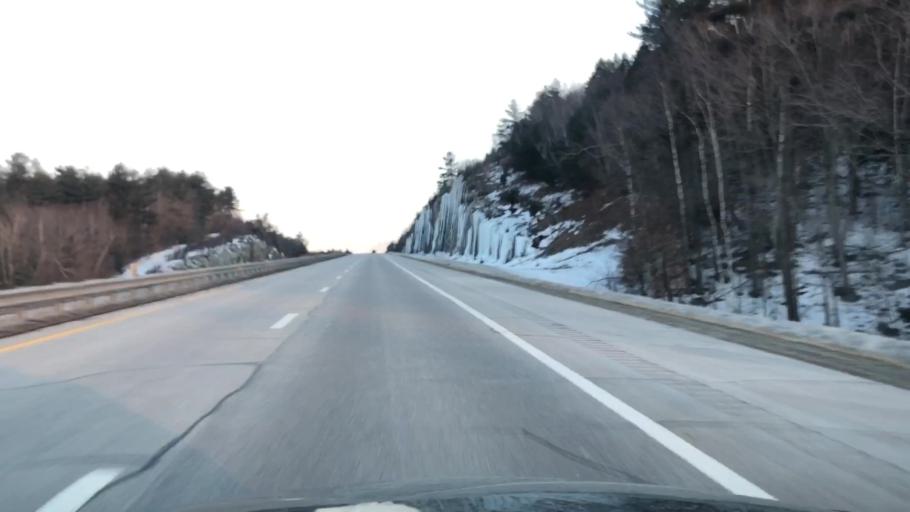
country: US
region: New Hampshire
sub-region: Merrimack County
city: New London
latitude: 43.4116
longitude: -72.0276
